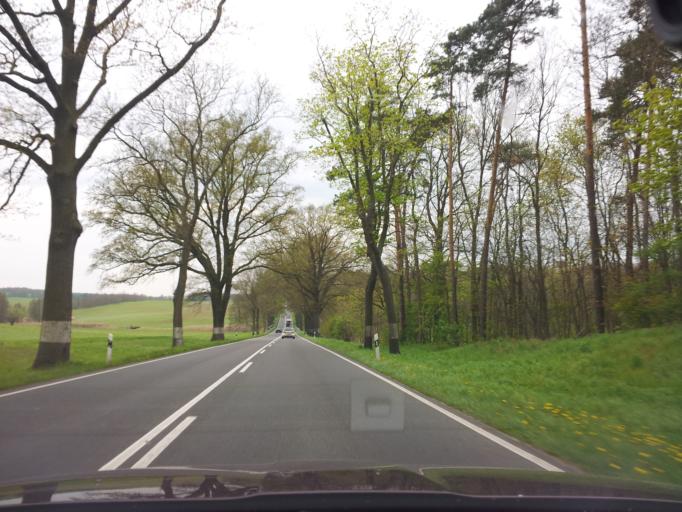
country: DE
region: Brandenburg
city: Neuhardenberg
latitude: 52.5092
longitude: 14.2578
